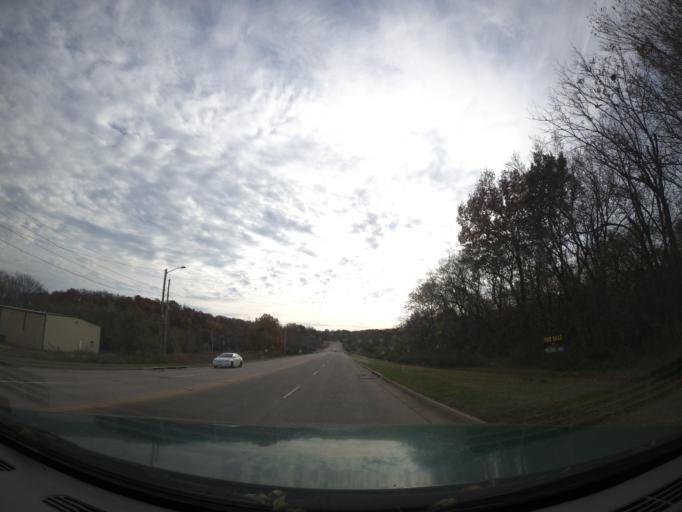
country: US
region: Oklahoma
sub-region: Tulsa County
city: Turley
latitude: 36.2172
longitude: -95.9942
